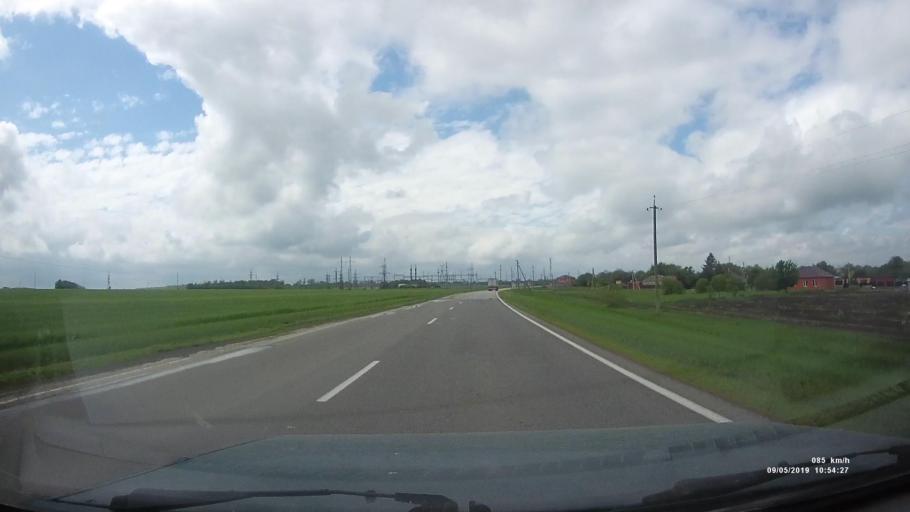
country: RU
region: Rostov
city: Peshkovo
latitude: 46.8776
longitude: 39.3304
